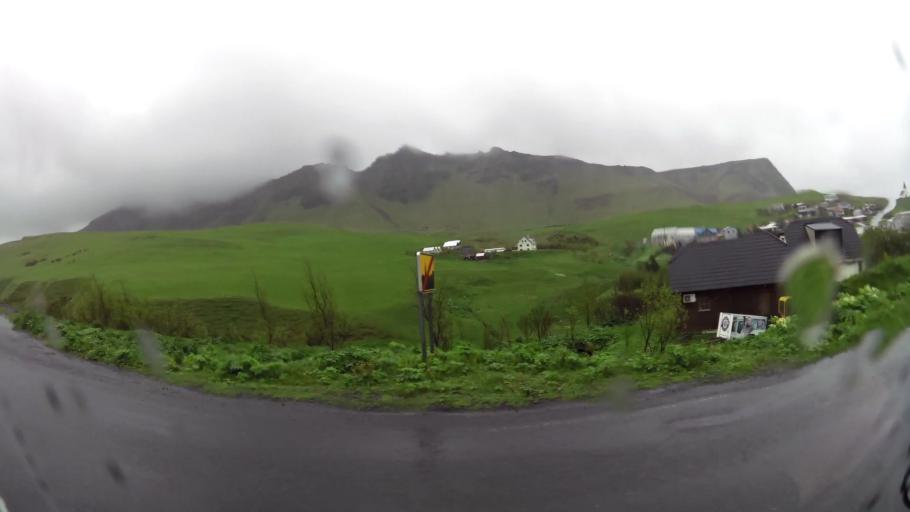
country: IS
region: South
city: Vestmannaeyjar
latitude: 63.4219
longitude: -19.0136
